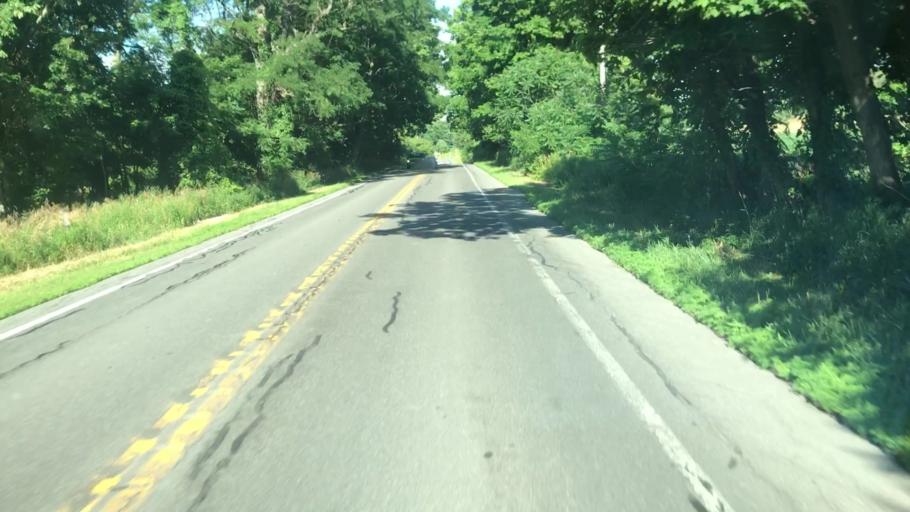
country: US
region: New York
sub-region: Onondaga County
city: Marcellus
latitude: 43.0182
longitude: -76.3830
